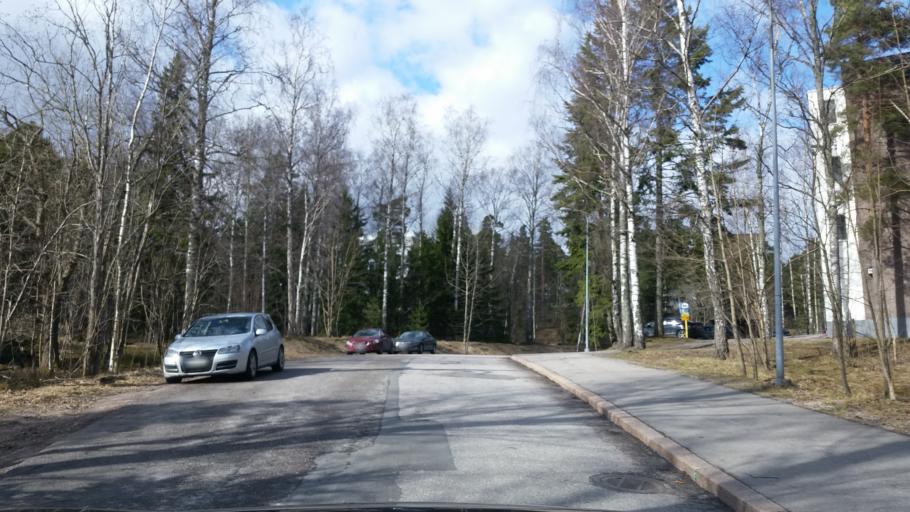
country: FI
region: Uusimaa
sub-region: Helsinki
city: Teekkarikylae
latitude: 60.1779
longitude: 24.8531
